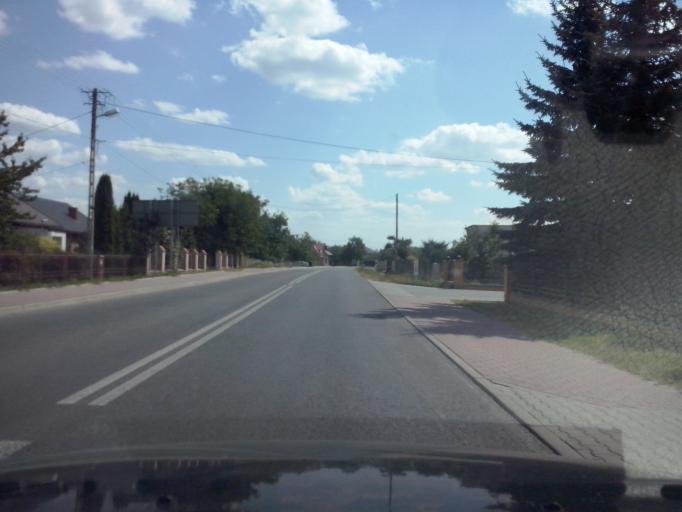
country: PL
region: Swietokrzyskie
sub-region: Powiat staszowski
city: Szydlow
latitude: 50.5908
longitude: 21.0079
